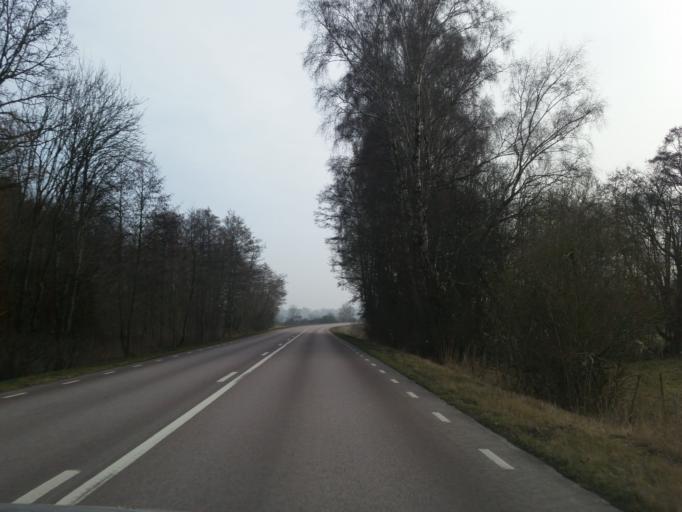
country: SE
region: Kalmar
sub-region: Borgholms Kommun
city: Borgholm
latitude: 57.1786
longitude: 17.0286
